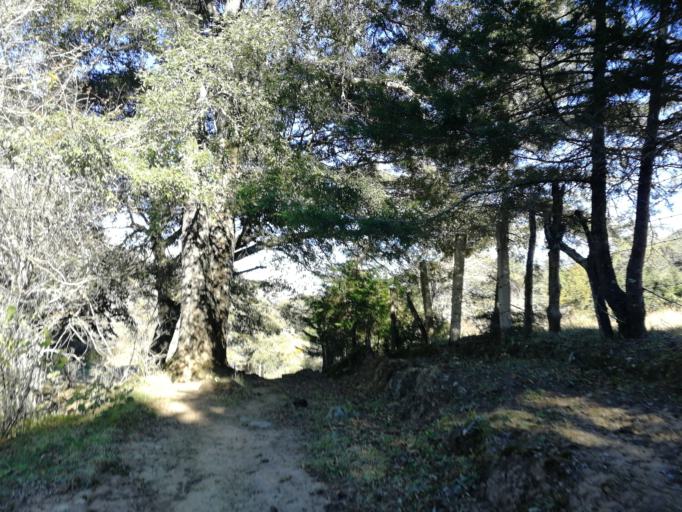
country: MX
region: San Luis Potosi
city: Zaragoza
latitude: 22.0167
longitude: -100.6101
